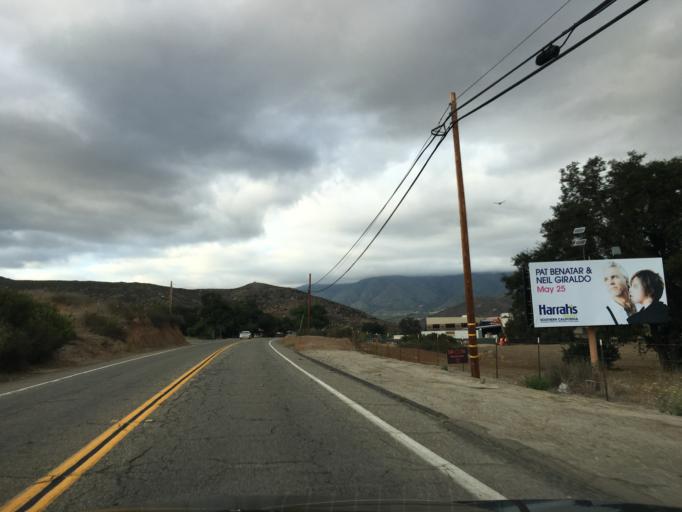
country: US
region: California
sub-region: San Diego County
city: Valley Center
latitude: 33.2495
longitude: -116.9633
